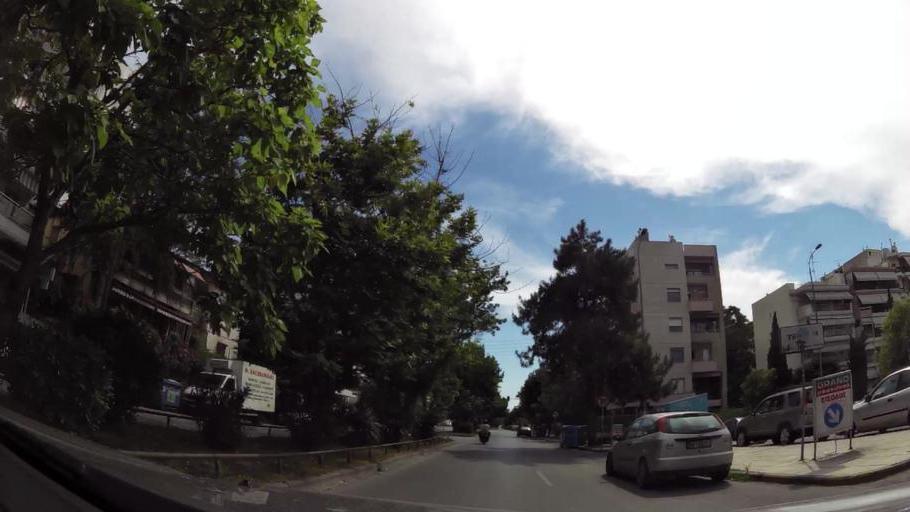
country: GR
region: Central Macedonia
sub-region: Nomos Thessalonikis
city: Kalamaria
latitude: 40.5855
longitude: 22.9470
